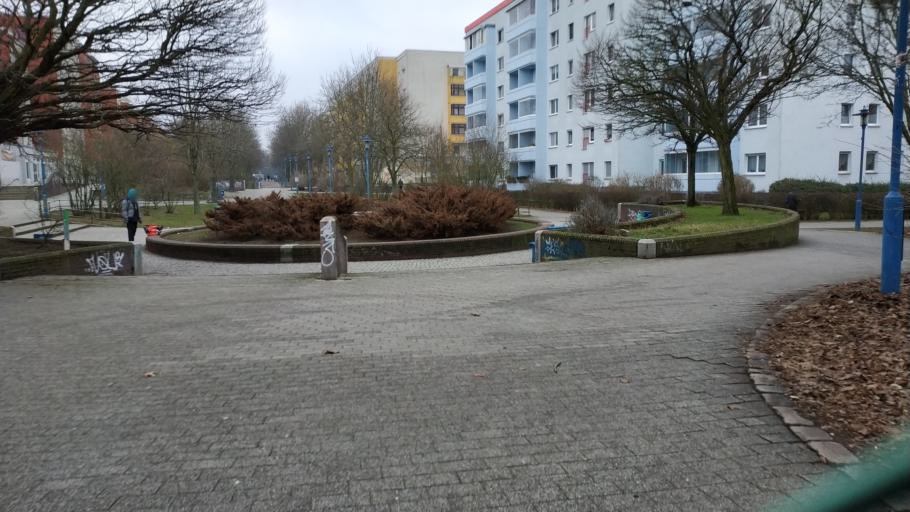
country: DE
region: Berlin
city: Hellersdorf
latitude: 52.5344
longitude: 13.6017
